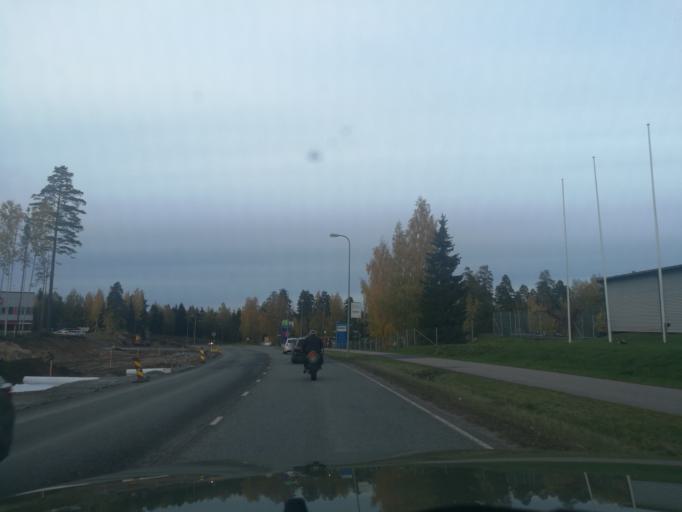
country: FI
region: Uusimaa
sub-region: Helsinki
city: Vantaa
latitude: 60.3061
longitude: 25.0944
